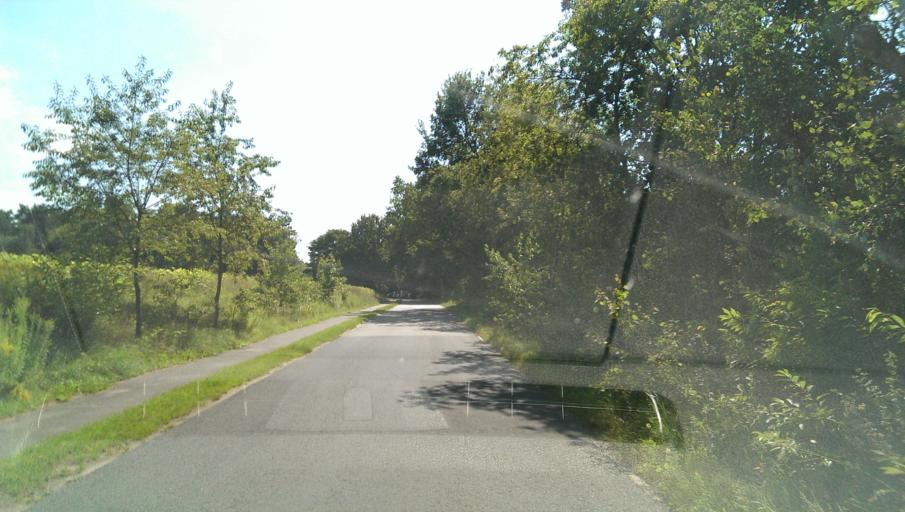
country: DE
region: Brandenburg
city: Michendorf
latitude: 52.2979
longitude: 13.0621
